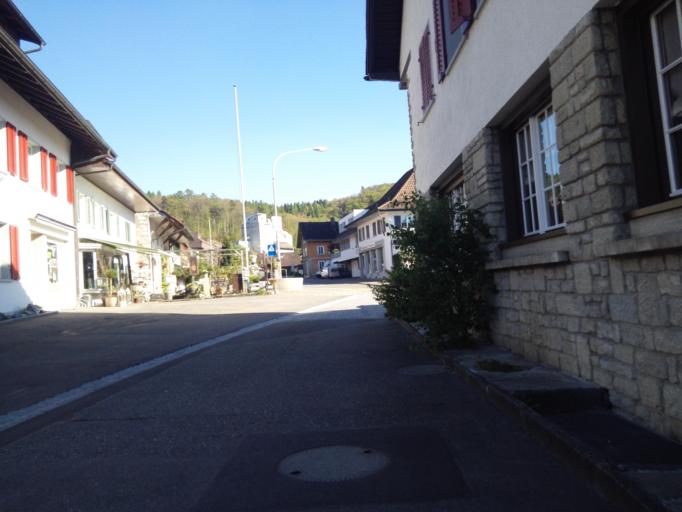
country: CH
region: Aargau
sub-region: Bezirk Baden
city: Wurenlingen
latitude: 47.5314
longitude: 8.2587
